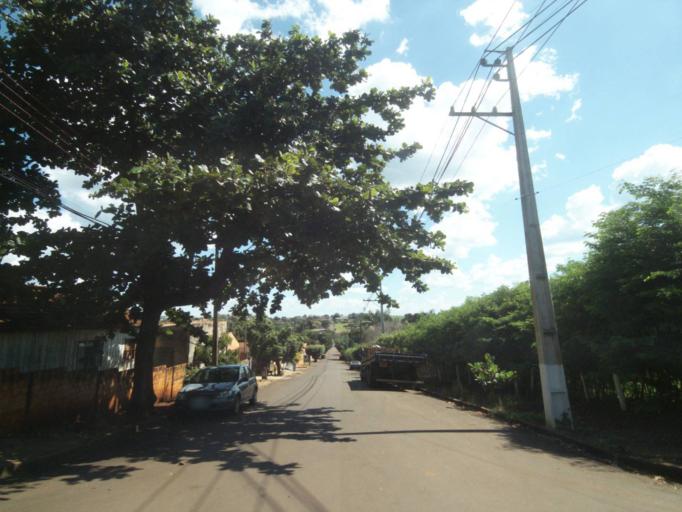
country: BR
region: Parana
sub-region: Sertanopolis
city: Sertanopolis
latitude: -23.0345
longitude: -50.8208
